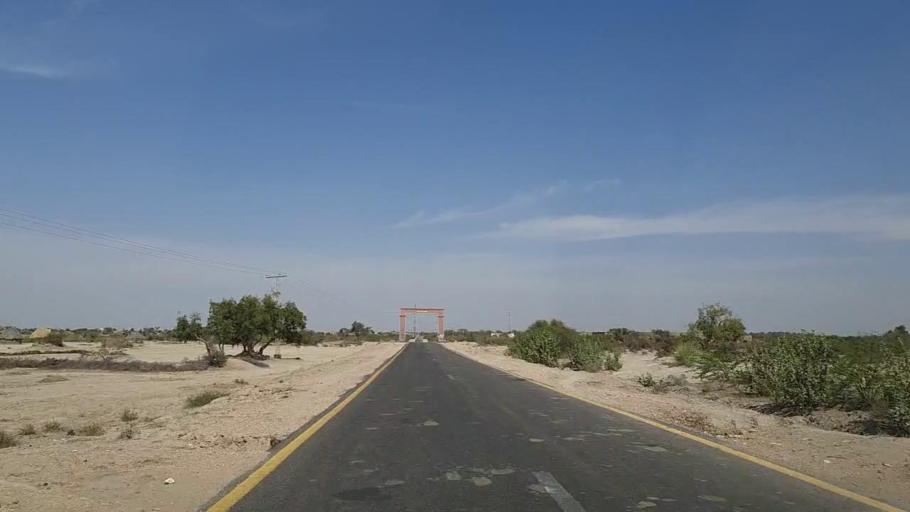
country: PK
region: Sindh
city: Mithi
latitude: 24.9665
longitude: 69.9123
